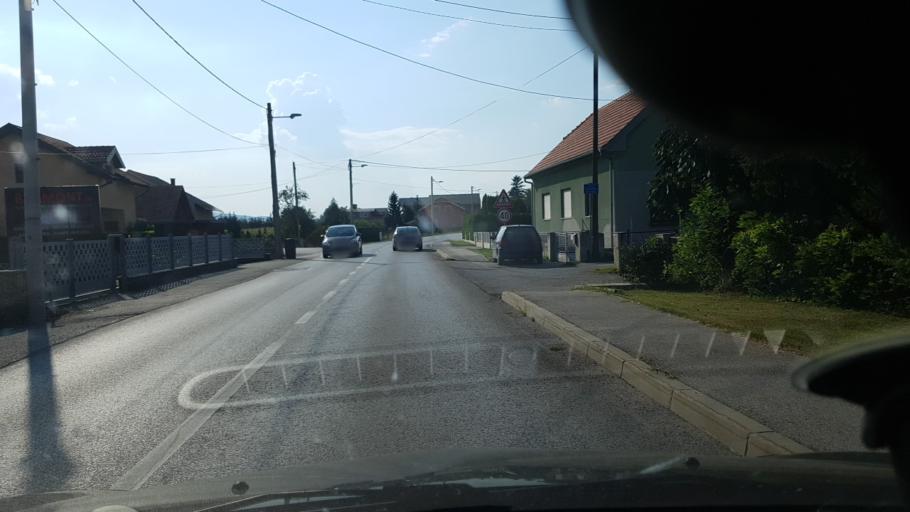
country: HR
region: Zagrebacka
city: Brdovec
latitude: 45.8667
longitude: 15.7632
